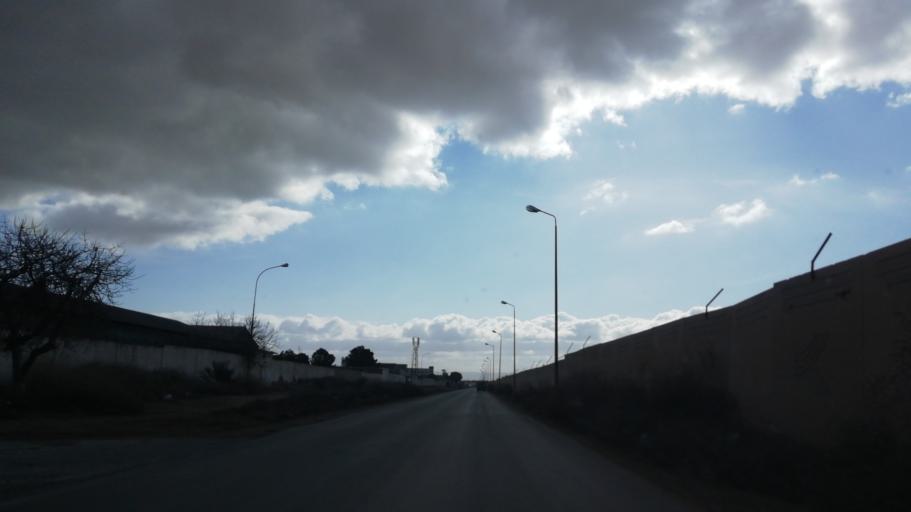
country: DZ
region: Oran
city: Es Senia
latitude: 35.6313
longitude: -0.5942
